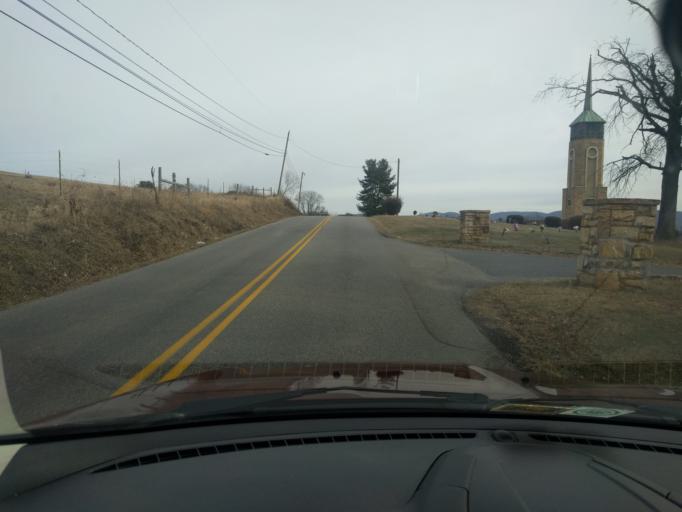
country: US
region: Virginia
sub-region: Augusta County
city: Fishersville
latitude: 38.0850
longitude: -78.9510
